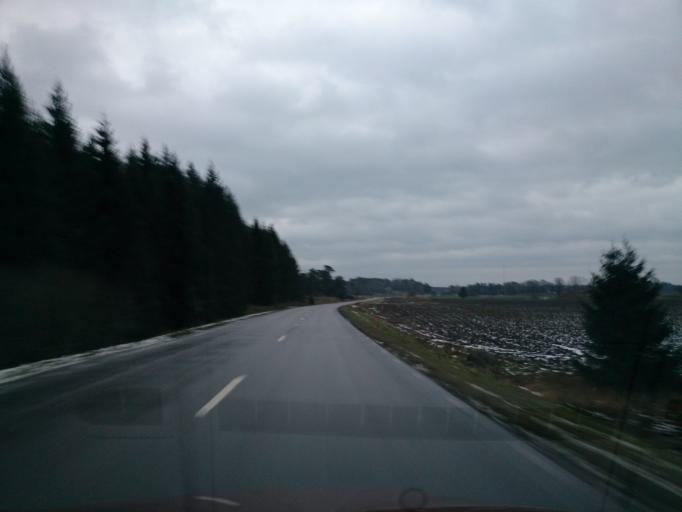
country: SE
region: OEstergoetland
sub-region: Linkopings Kommun
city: Linghem
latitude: 58.4119
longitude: 15.8928
